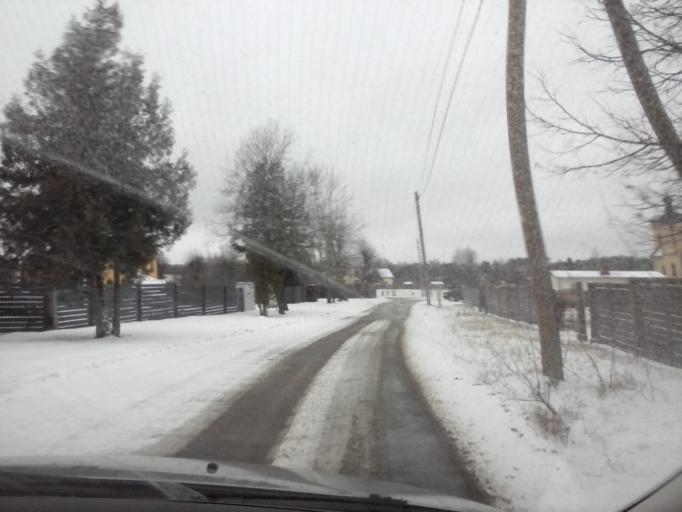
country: LV
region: Valkas Rajons
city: Valka
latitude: 57.7783
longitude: 26.0190
